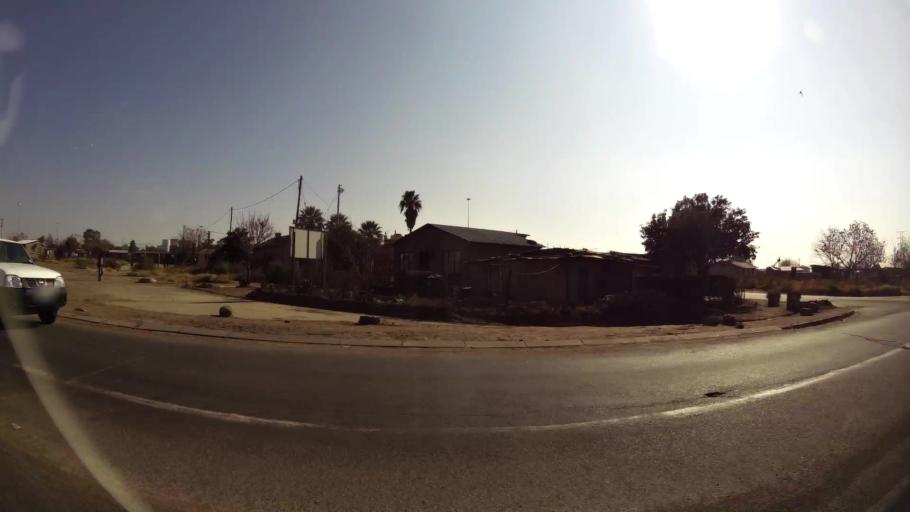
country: ZA
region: Orange Free State
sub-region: Mangaung Metropolitan Municipality
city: Bloemfontein
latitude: -29.1338
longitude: 26.2339
